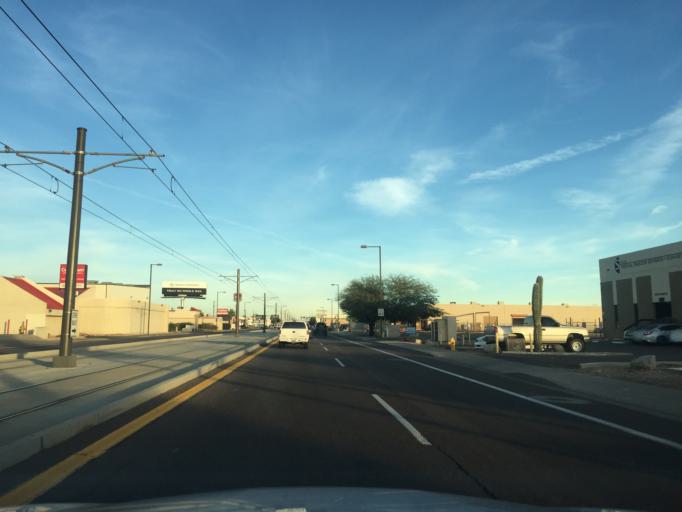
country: US
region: Arizona
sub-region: Maricopa County
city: Phoenix
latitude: 33.4481
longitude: -112.0164
